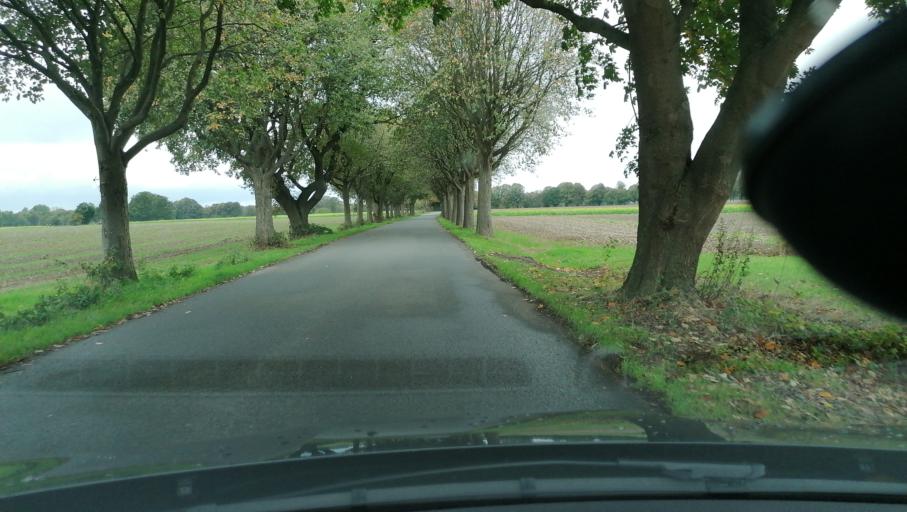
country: DE
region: North Rhine-Westphalia
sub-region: Regierungsbezirk Munster
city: Recklinghausen
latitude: 51.6298
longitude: 7.1804
